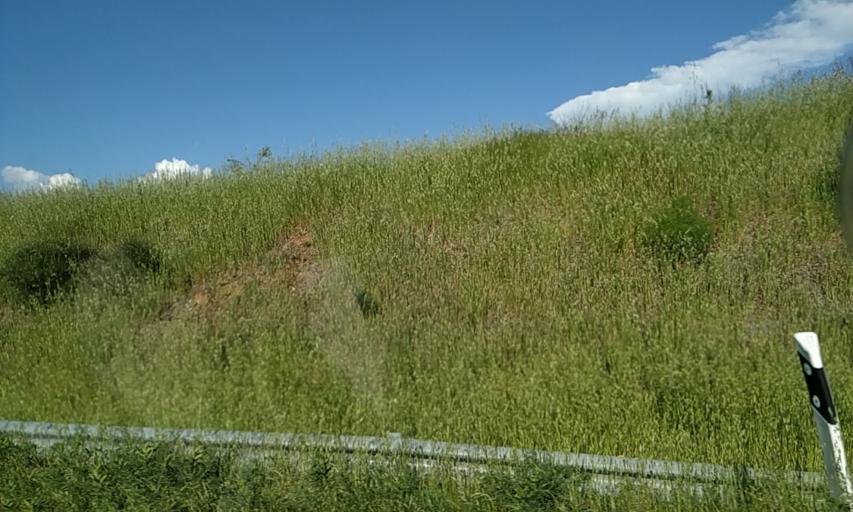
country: PT
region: Portalegre
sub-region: Portalegre
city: Urra
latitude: 39.0920
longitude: -7.4374
